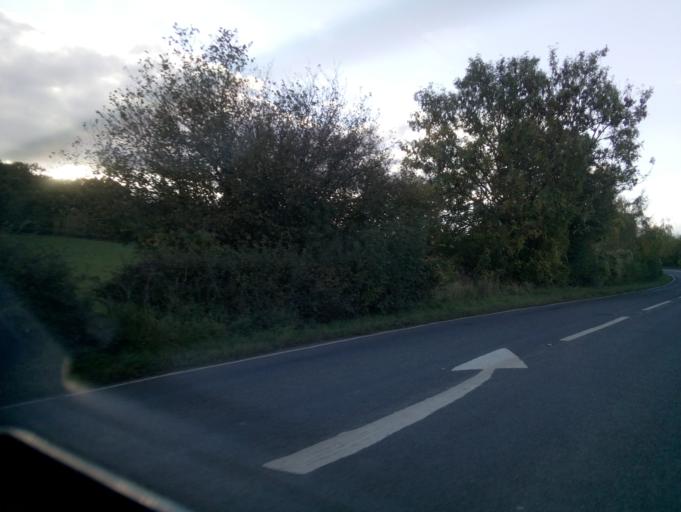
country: GB
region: England
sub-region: Herefordshire
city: Ledbury
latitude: 52.0503
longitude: -2.4496
